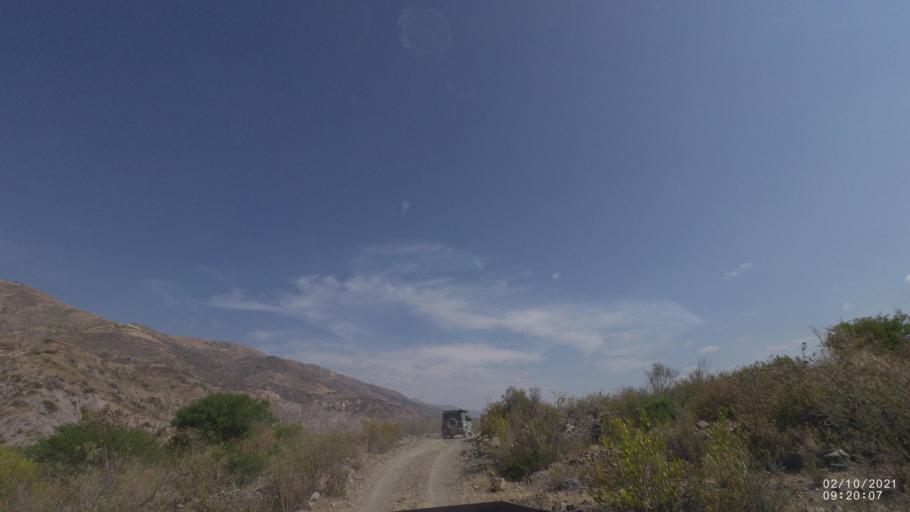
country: BO
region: Cochabamba
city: Irpa Irpa
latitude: -17.8746
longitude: -66.3072
